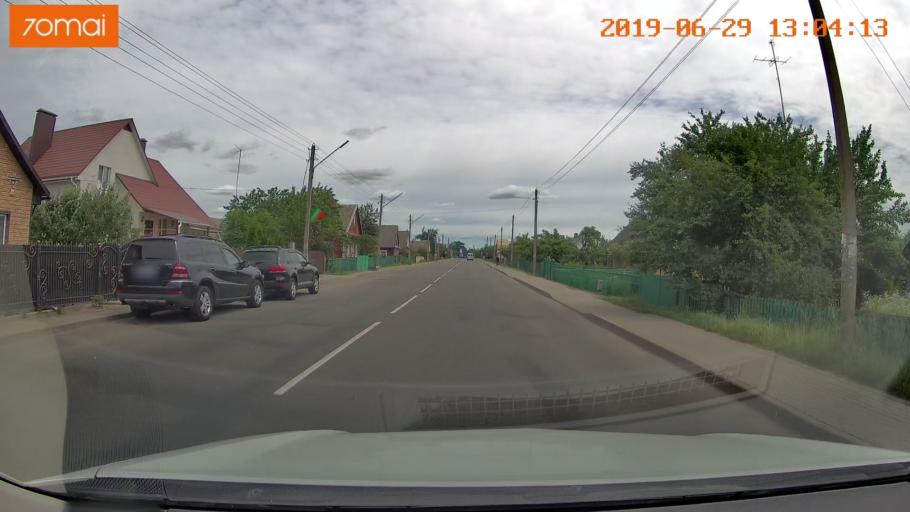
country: BY
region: Minsk
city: Slutsk
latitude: 53.0310
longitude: 27.5691
